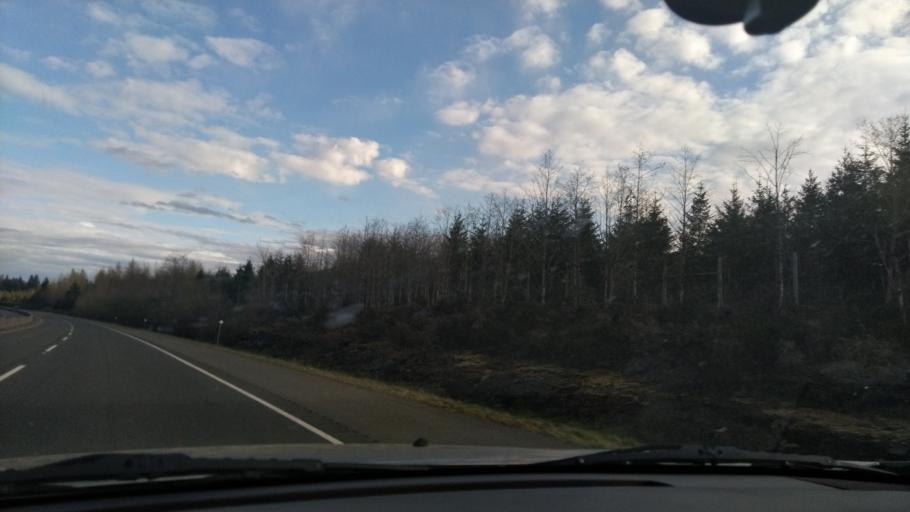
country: CA
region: British Columbia
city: Courtenay
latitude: 49.7781
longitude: -125.1410
